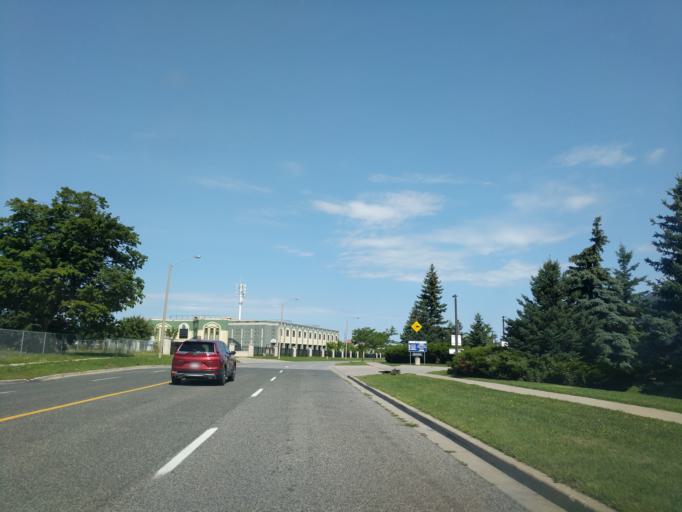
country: CA
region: Ontario
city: Scarborough
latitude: 43.8177
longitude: -79.2284
